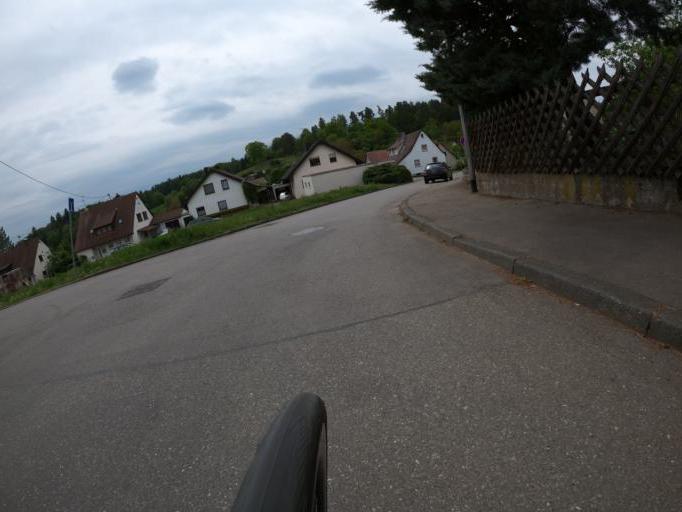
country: DE
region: Baden-Wuerttemberg
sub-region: Regierungsbezirk Stuttgart
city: Aidlingen
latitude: 48.7004
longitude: 8.8890
